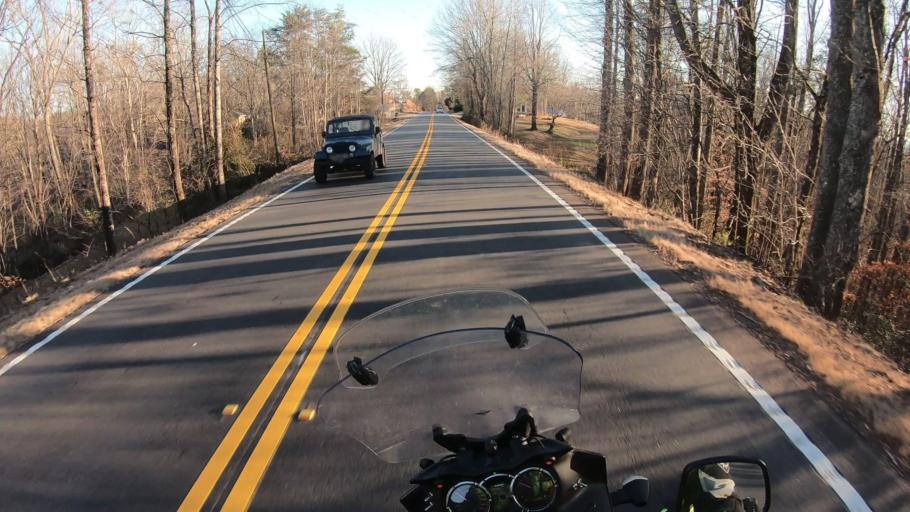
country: US
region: Georgia
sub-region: Lumpkin County
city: Dahlonega
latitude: 34.5962
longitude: -83.9696
